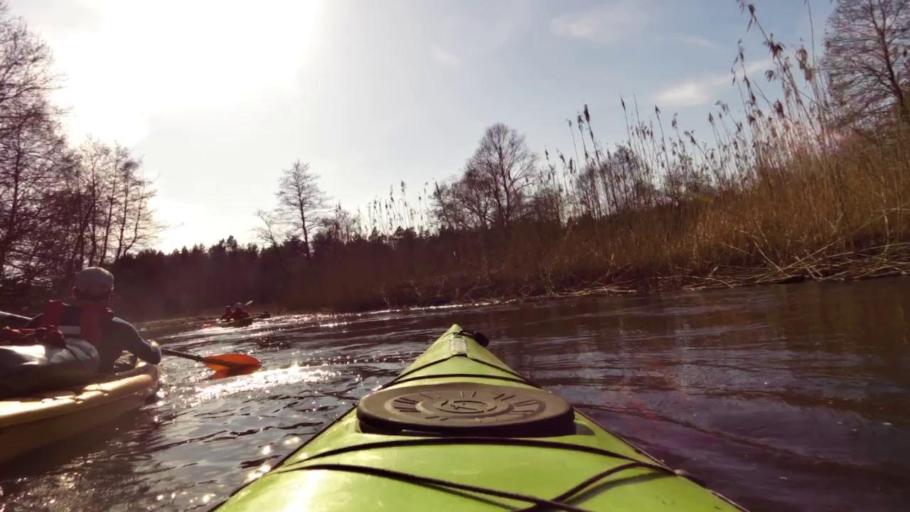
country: PL
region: West Pomeranian Voivodeship
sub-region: Powiat lobeski
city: Lobez
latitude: 53.7017
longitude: 15.5555
